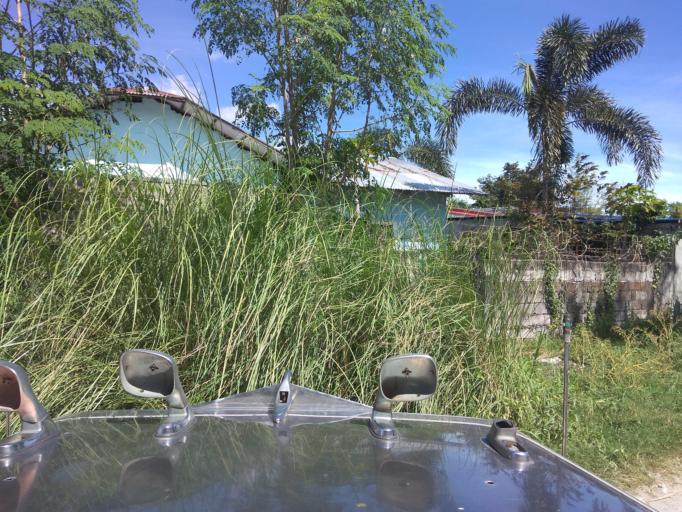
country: PH
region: Central Luzon
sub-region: Province of Pampanga
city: Magliman
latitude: 15.0368
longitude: 120.6608
